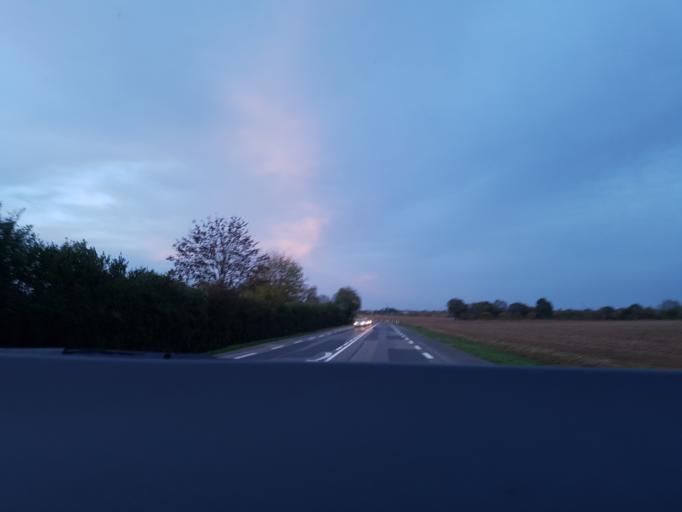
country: FR
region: Pays de la Loire
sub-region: Departement de la Mayenne
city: Ahuille
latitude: 47.9754
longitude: -0.8726
